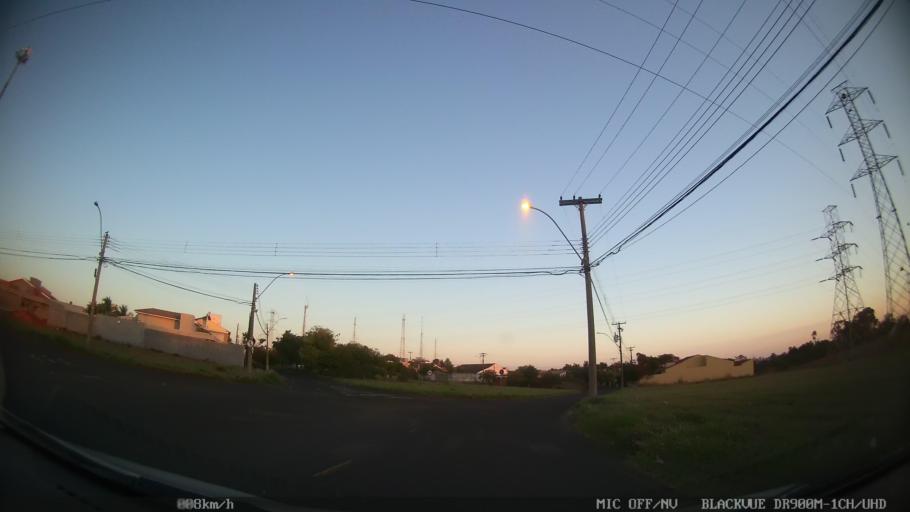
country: BR
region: Sao Paulo
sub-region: Sao Jose Do Rio Preto
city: Sao Jose do Rio Preto
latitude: -20.7977
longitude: -49.3497
